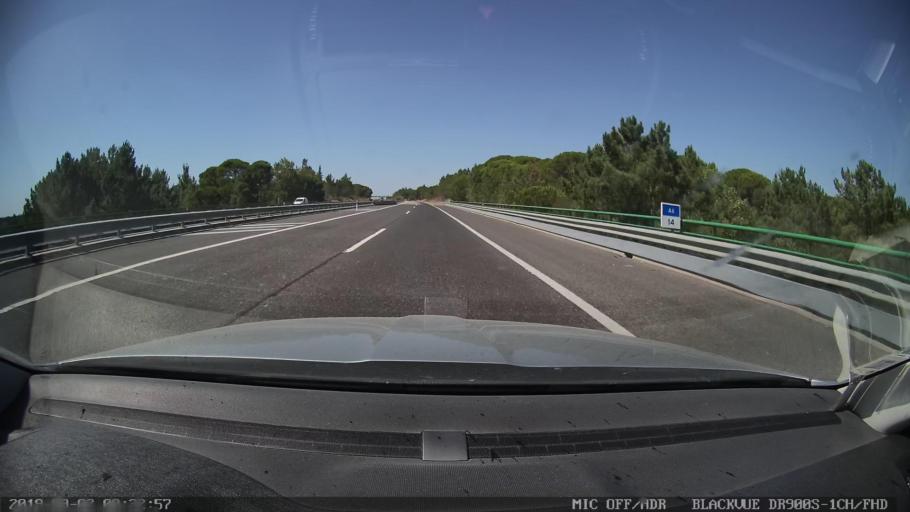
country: PT
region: Evora
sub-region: Vendas Novas
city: Vendas Novas
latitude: 38.6401
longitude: -8.4966
